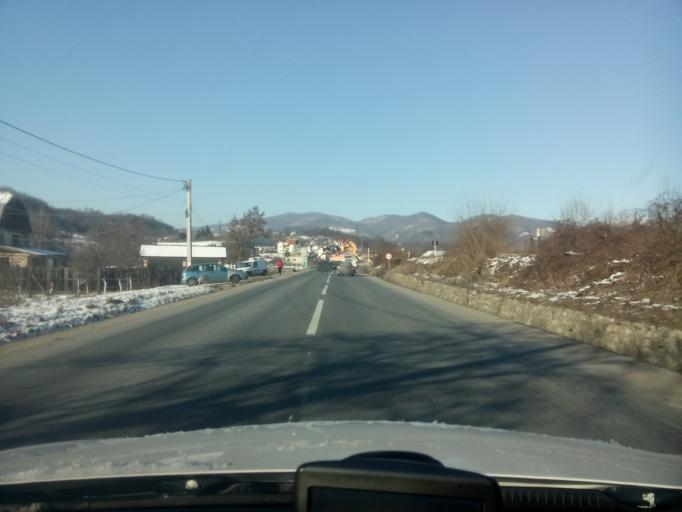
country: RO
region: Valcea
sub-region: Comuna Bujoreni
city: Bujoreni
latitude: 45.1666
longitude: 24.3682
